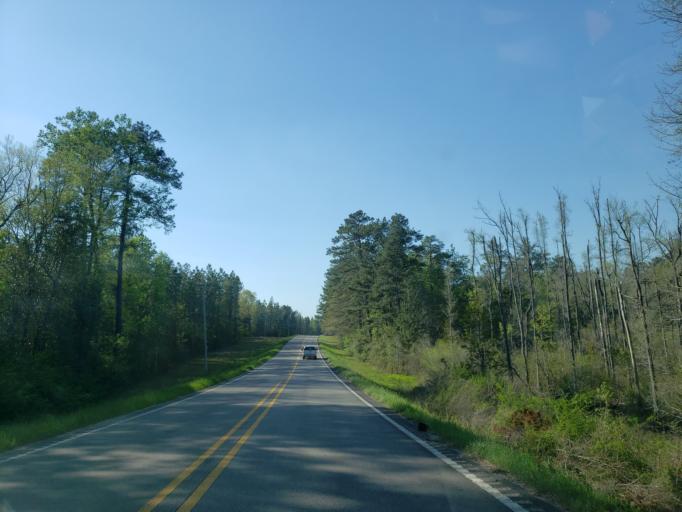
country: US
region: Mississippi
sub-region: Perry County
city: Richton
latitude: 31.4470
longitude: -88.9741
